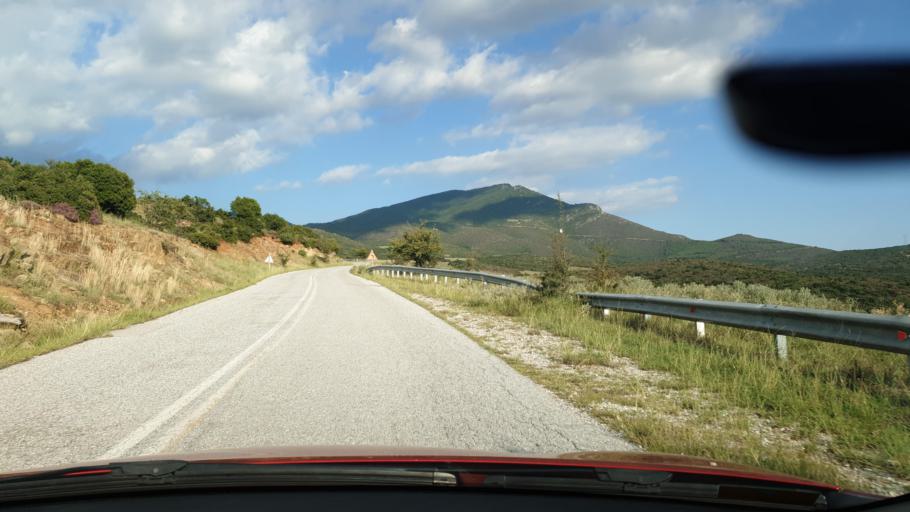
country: GR
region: Central Macedonia
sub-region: Nomos Thessalonikis
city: Peristera
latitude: 40.5117
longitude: 23.1656
